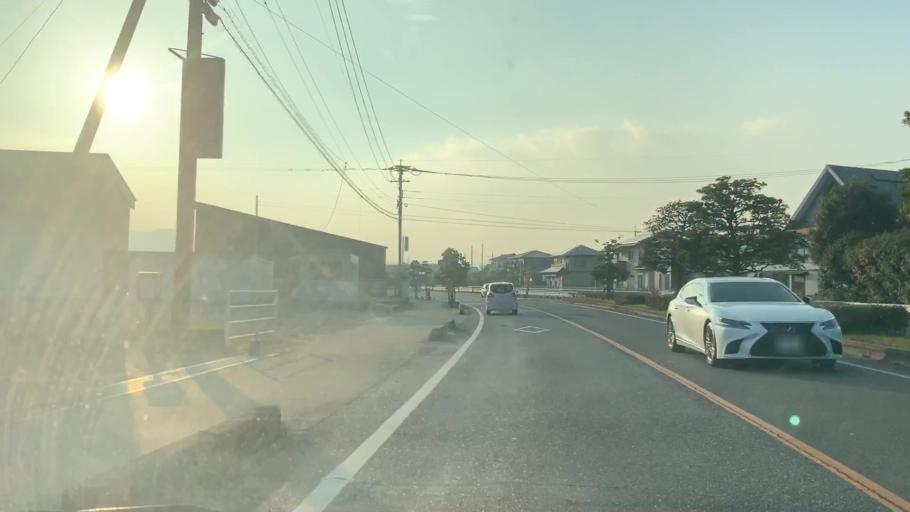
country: JP
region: Saga Prefecture
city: Saga-shi
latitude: 33.2804
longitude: 130.1538
